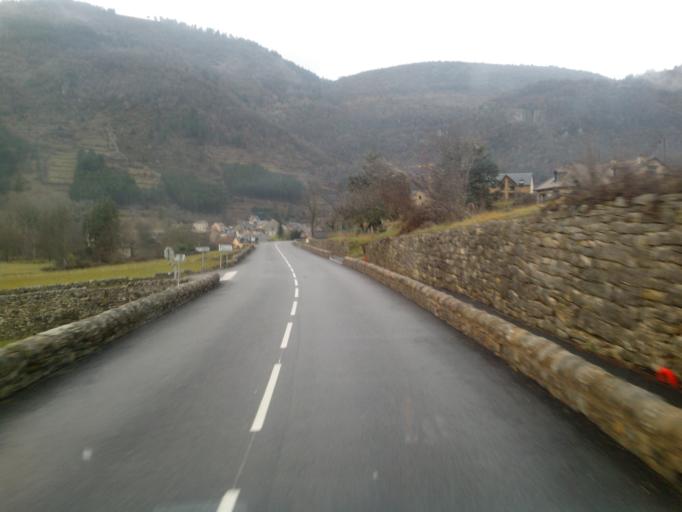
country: FR
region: Languedoc-Roussillon
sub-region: Departement de la Lozere
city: Florac
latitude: 44.3756
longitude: 3.5282
